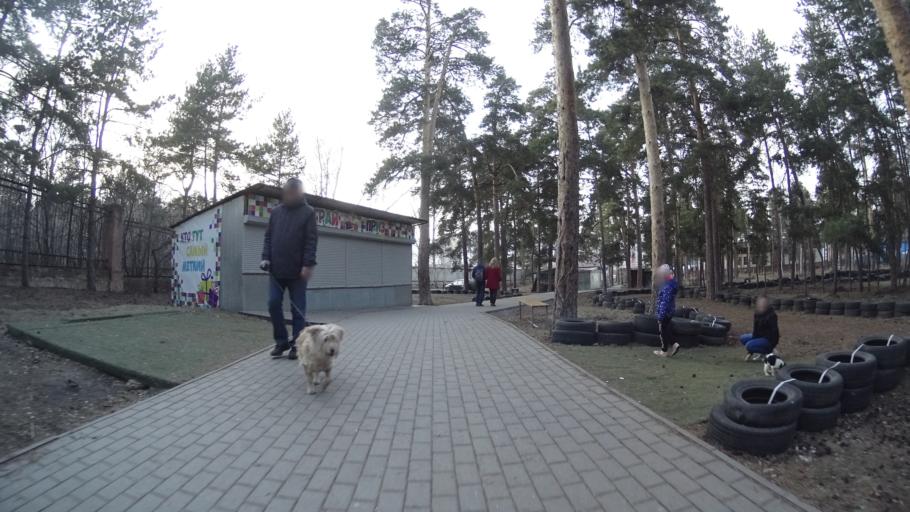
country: RU
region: Chelyabinsk
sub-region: Gorod Chelyabinsk
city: Chelyabinsk
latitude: 55.1664
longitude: 61.3703
